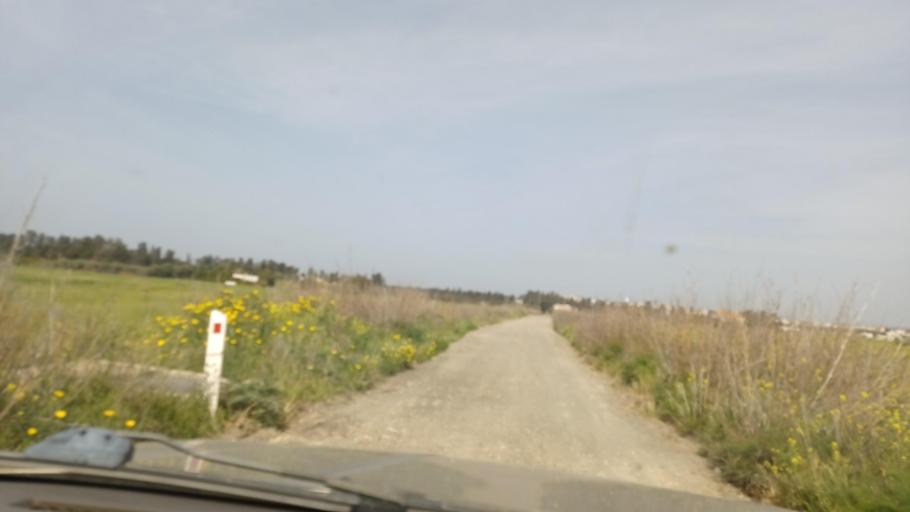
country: CY
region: Pafos
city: Paphos
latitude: 34.7431
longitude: 32.4642
